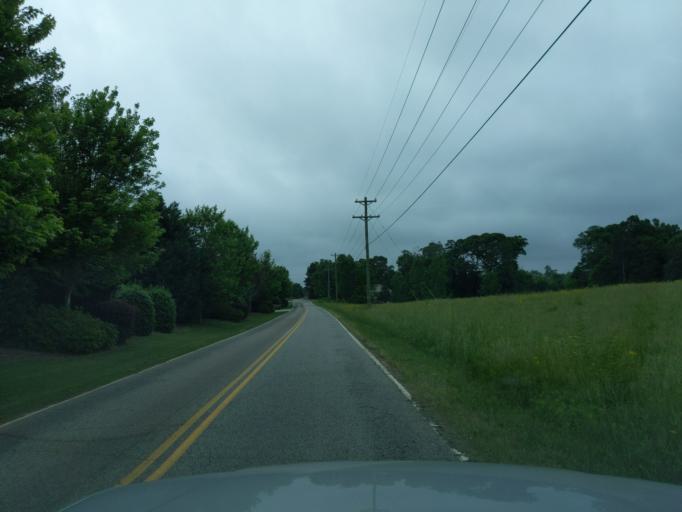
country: US
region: South Carolina
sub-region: Greenville County
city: Five Forks
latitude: 34.8576
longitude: -82.2161
